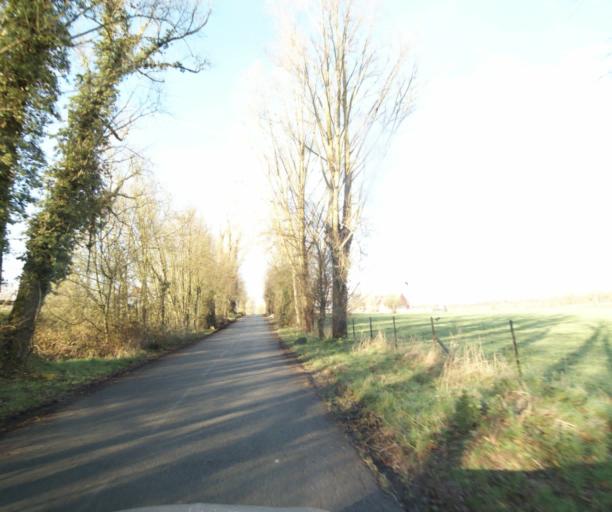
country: FR
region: Nord-Pas-de-Calais
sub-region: Departement du Nord
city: Curgies
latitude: 50.3304
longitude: 3.5929
